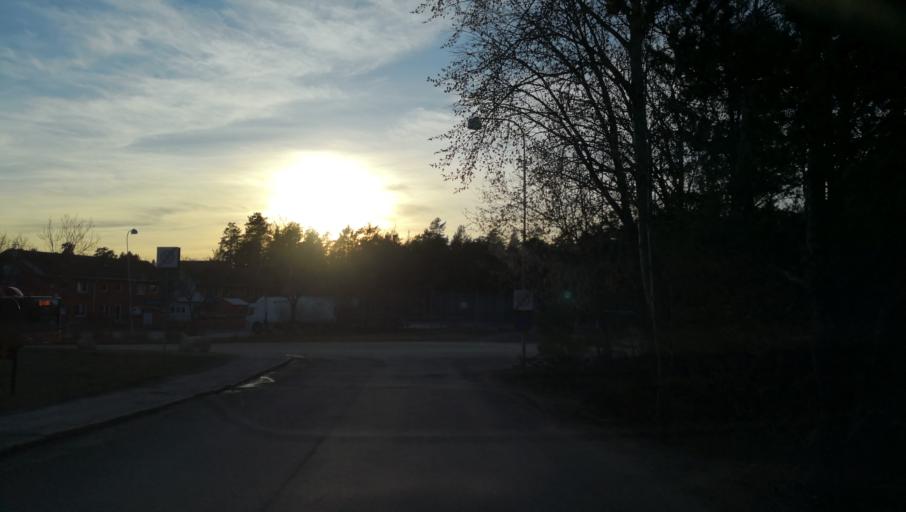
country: SE
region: Stockholm
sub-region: Varmdo Kommun
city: Gustavsberg
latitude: 59.3391
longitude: 18.3953
